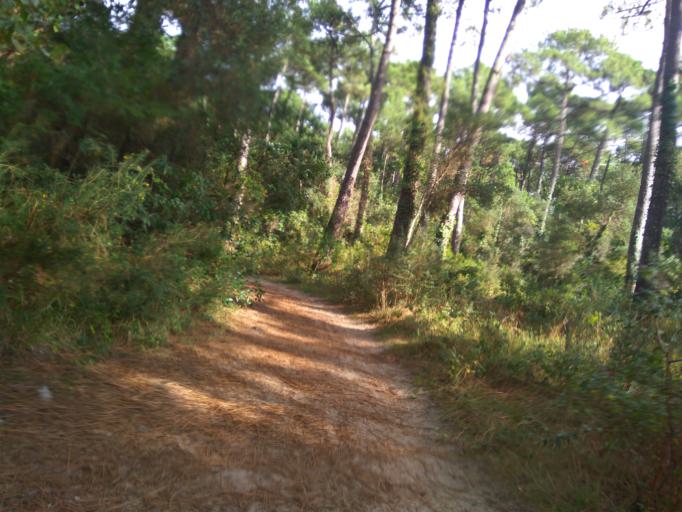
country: FR
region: Aquitaine
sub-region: Departement des Landes
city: Capbreton
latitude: 43.6324
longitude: -1.4442
